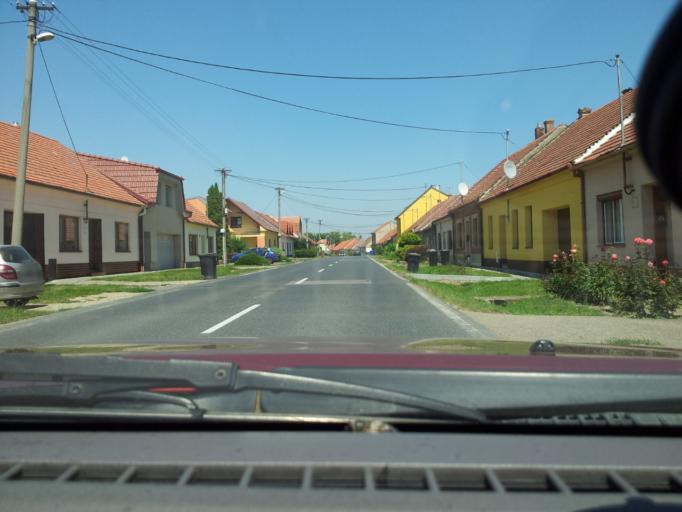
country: CZ
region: South Moravian
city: Telnice
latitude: 49.0984
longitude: 16.7170
